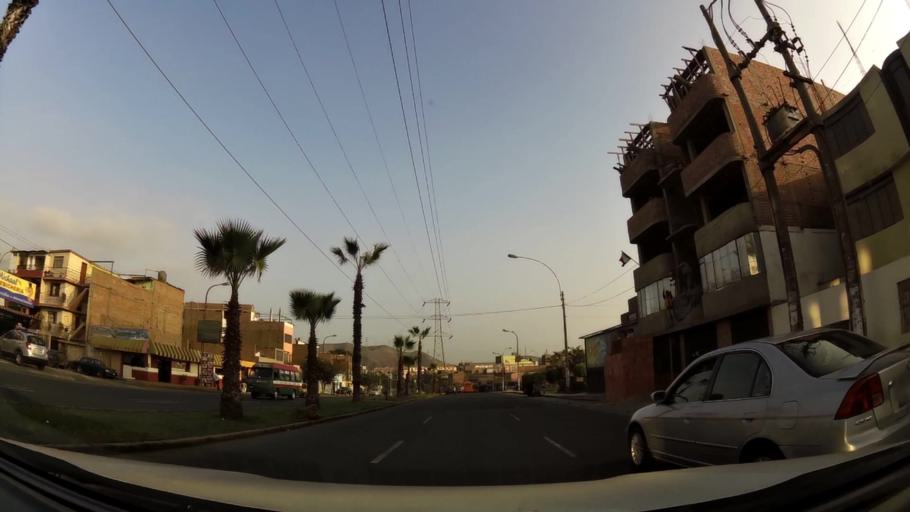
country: PE
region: Lima
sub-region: Lima
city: Independencia
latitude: -11.9853
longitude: -77.0723
